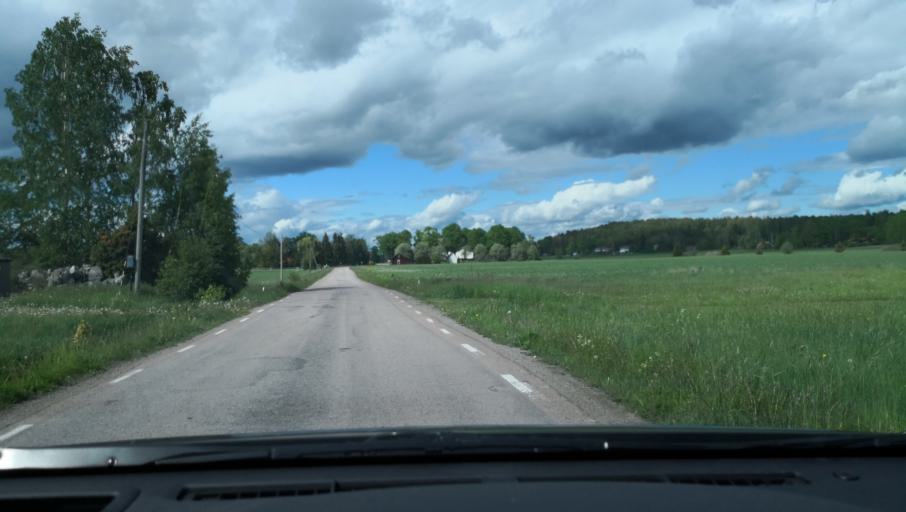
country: SE
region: Vaestmanland
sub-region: Hallstahammars Kommun
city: Kolback
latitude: 59.5449
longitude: 16.3109
